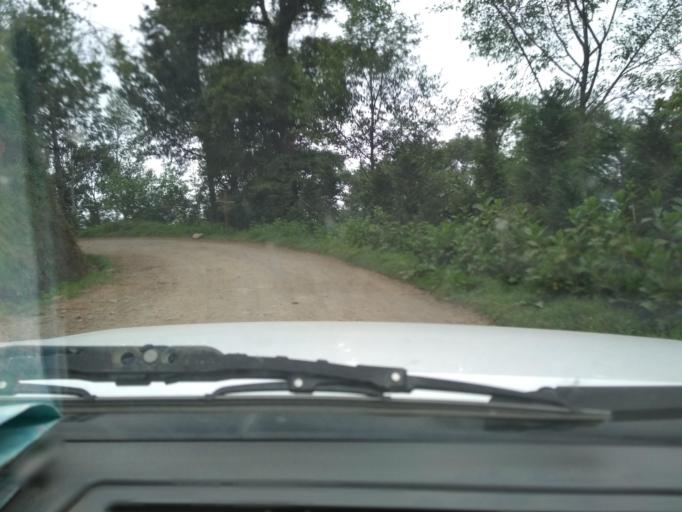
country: MX
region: Veracruz
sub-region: La Perla
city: Chilapa
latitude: 18.9985
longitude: -97.1660
